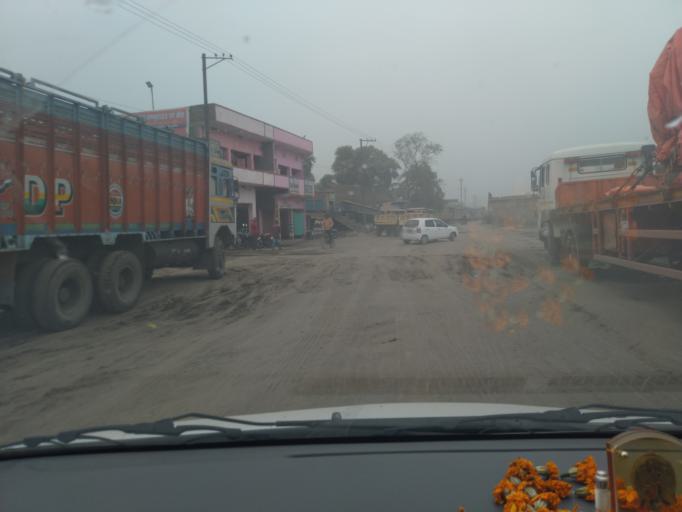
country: IN
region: Bihar
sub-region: Rohtas
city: Dehri
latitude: 24.9147
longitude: 84.1596
